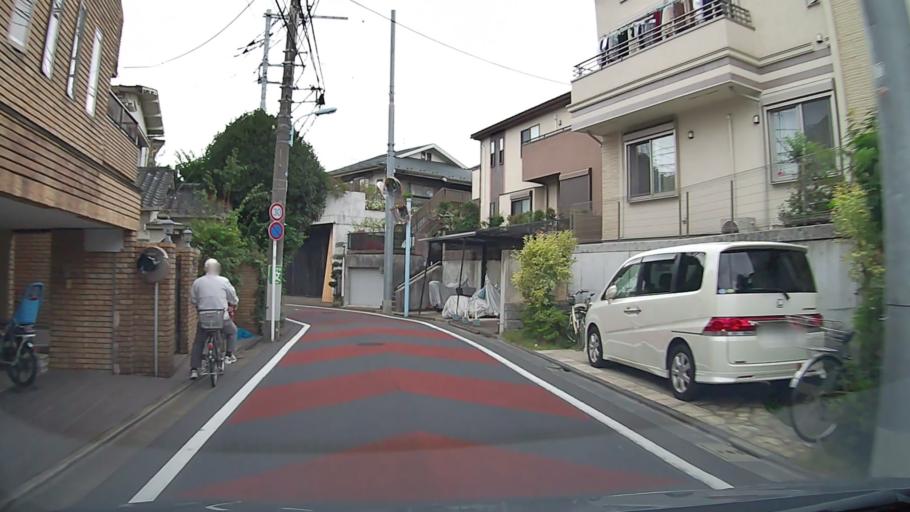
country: JP
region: Tokyo
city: Tokyo
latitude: 35.6902
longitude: 139.6304
